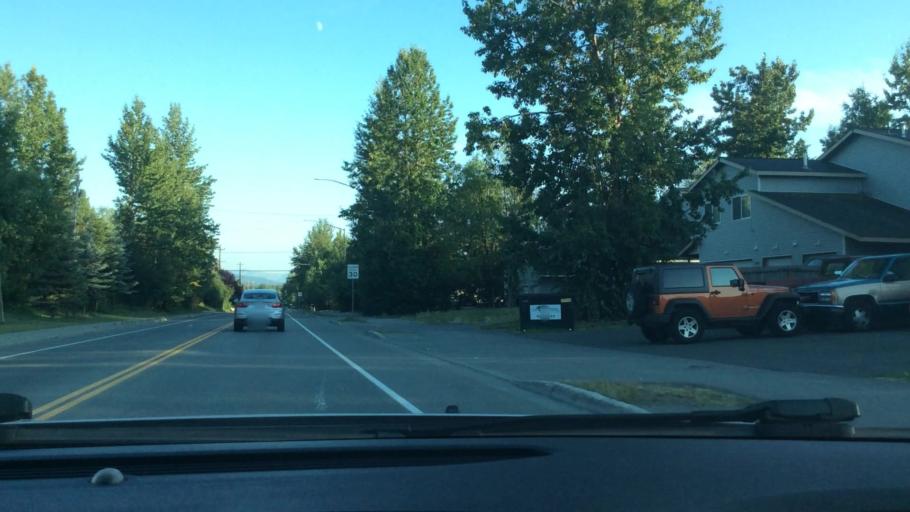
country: US
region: Alaska
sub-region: Anchorage Municipality
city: Elmendorf Air Force Base
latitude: 61.2181
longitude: -149.7560
